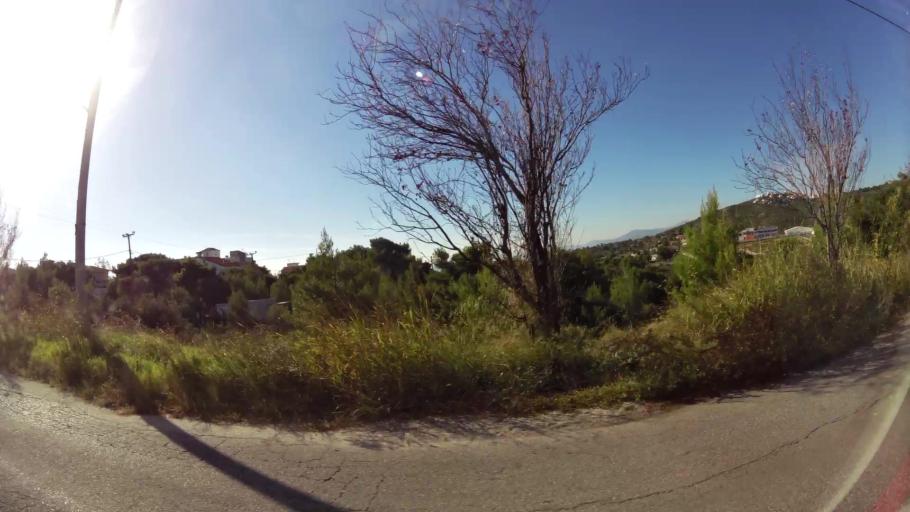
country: GR
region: Attica
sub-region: Nomarchia Anatolikis Attikis
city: Anthousa
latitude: 38.0338
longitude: 23.8796
